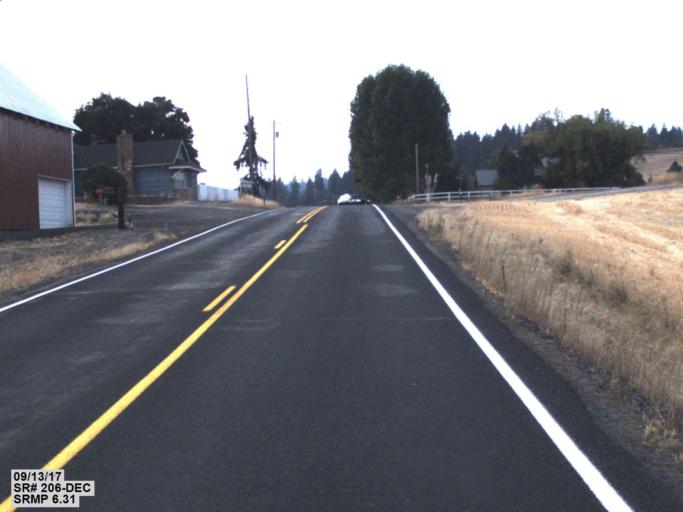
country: US
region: Washington
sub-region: Spokane County
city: Trentwood
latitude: 47.8022
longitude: -117.2275
